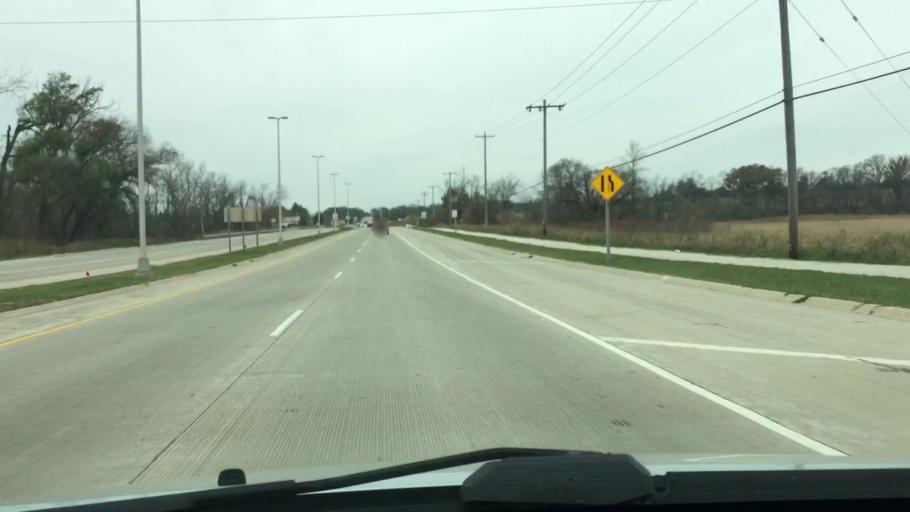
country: US
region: Wisconsin
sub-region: Milwaukee County
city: Franklin
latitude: 42.8728
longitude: -87.9919
